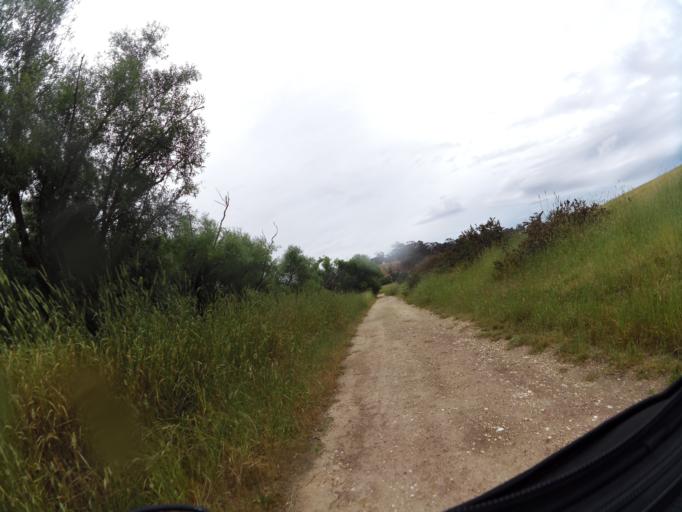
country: AU
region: Victoria
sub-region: Mount Alexander
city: Castlemaine
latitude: -37.2110
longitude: 144.0262
